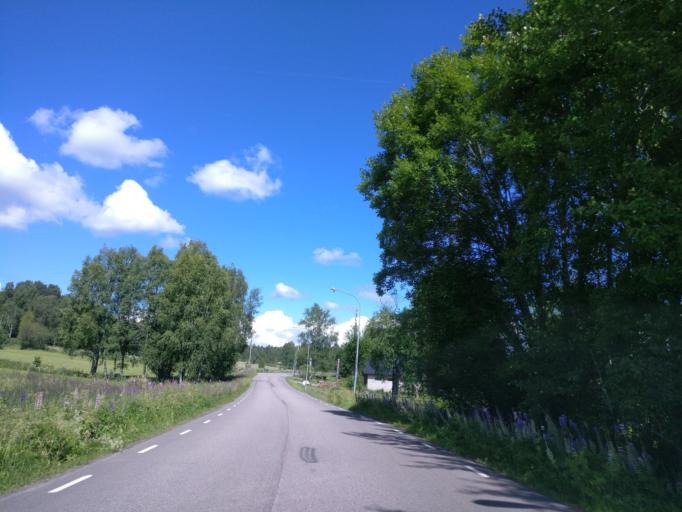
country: SE
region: Vaermland
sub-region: Hagfors Kommun
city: Hagfors
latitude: 60.0347
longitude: 13.6291
